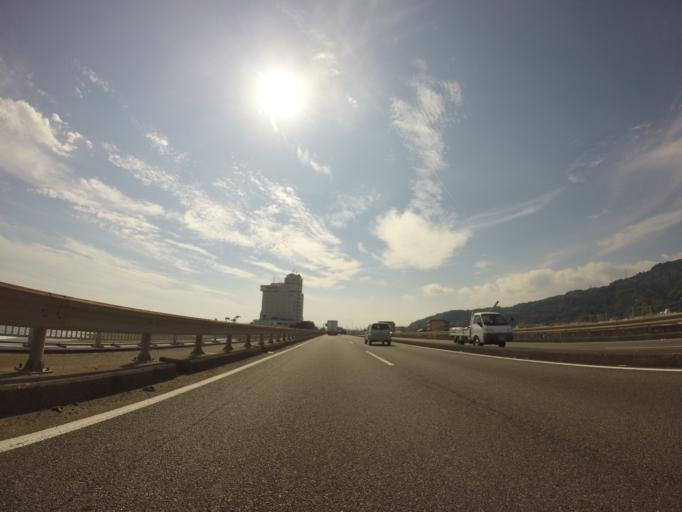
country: JP
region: Shizuoka
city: Shizuoka-shi
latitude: 35.0590
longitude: 138.5347
